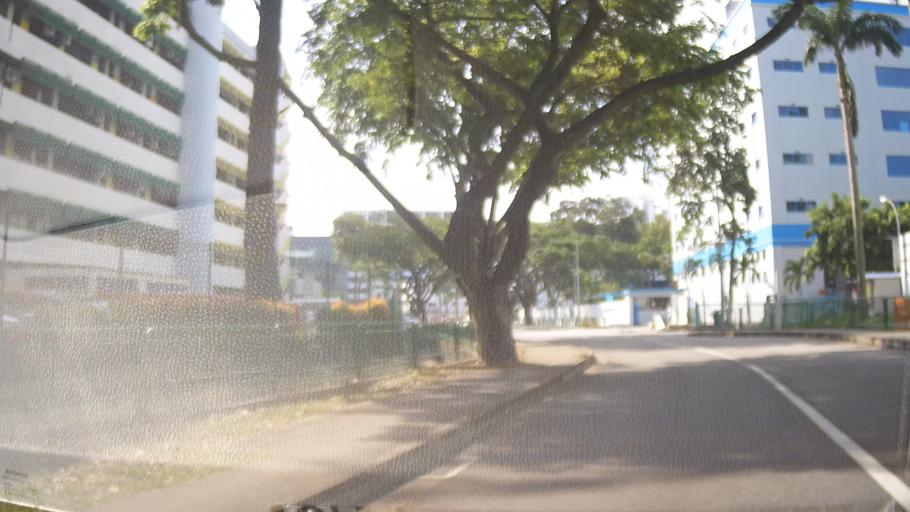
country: SG
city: Singapore
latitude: 1.3167
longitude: 103.8671
